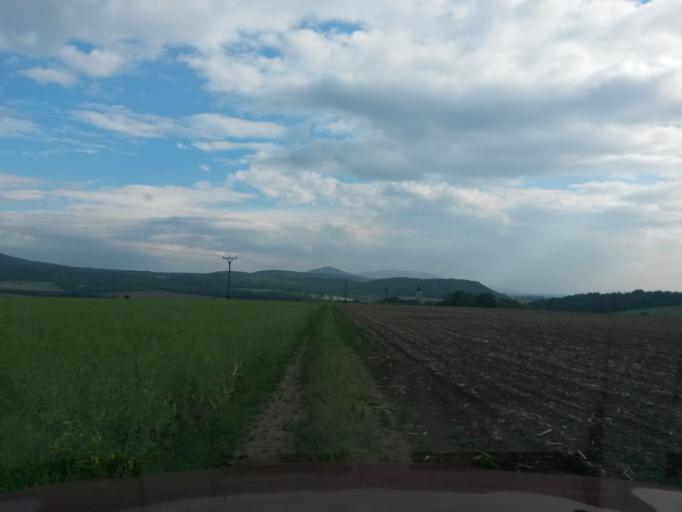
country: SK
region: Kosicky
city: Secovce
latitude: 48.7429
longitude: 21.4611
